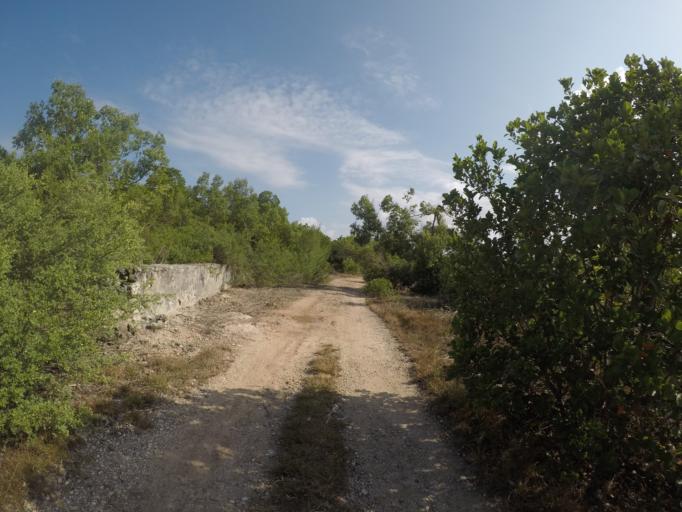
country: TZ
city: Kiwengwa
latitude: -6.1443
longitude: 39.4900
